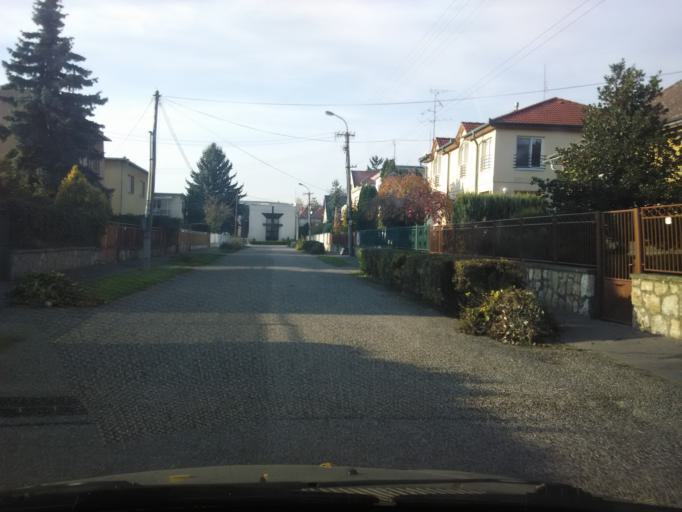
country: SK
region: Nitriansky
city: Levice
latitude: 48.2192
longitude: 18.6149
